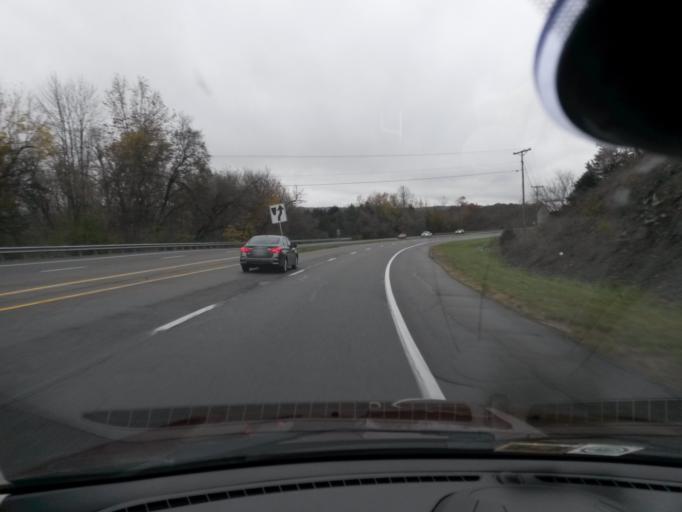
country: US
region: Virginia
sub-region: Botetourt County
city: Fincastle
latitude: 37.5147
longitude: -79.8813
